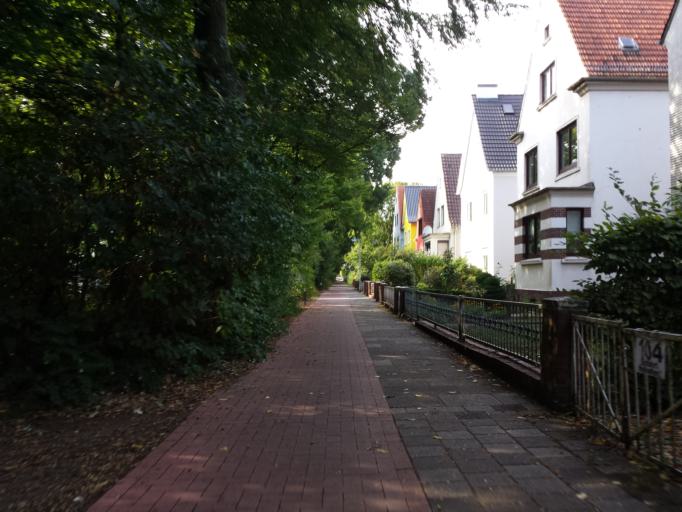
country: DE
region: Bremen
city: Bremen
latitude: 53.0604
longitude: 8.7917
